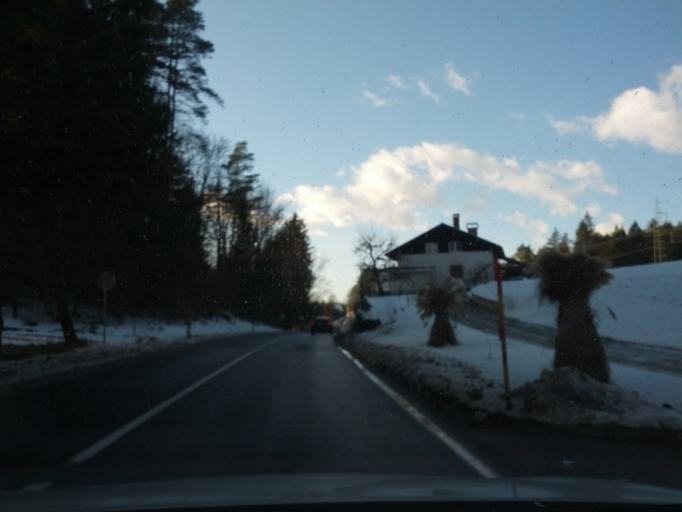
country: SI
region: Moravce
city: Moravce
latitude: 46.1376
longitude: 14.7338
